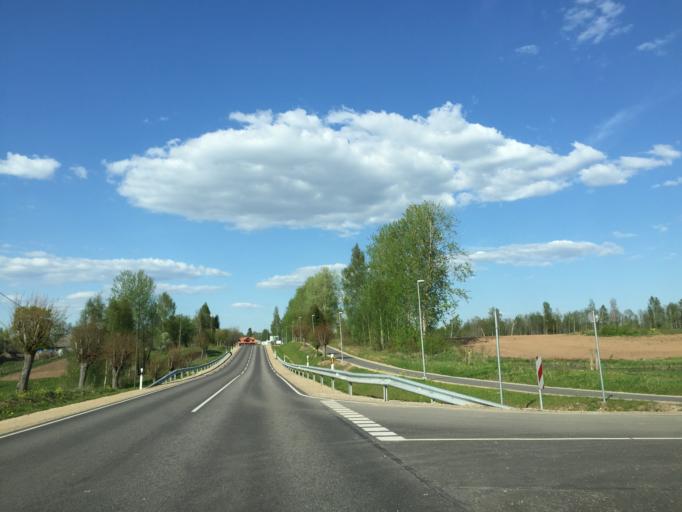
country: LV
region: Limbazu Rajons
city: Limbazi
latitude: 57.4990
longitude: 24.7126
